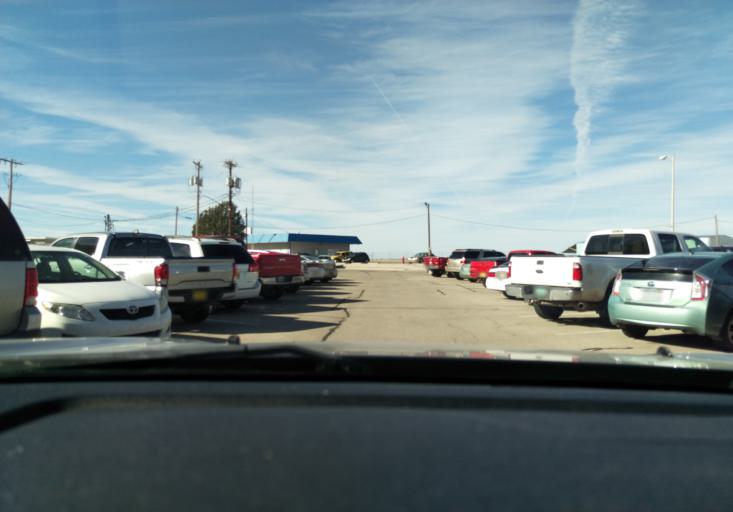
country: US
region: New Mexico
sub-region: Lea County
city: Hobbs
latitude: 32.6927
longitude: -103.2144
